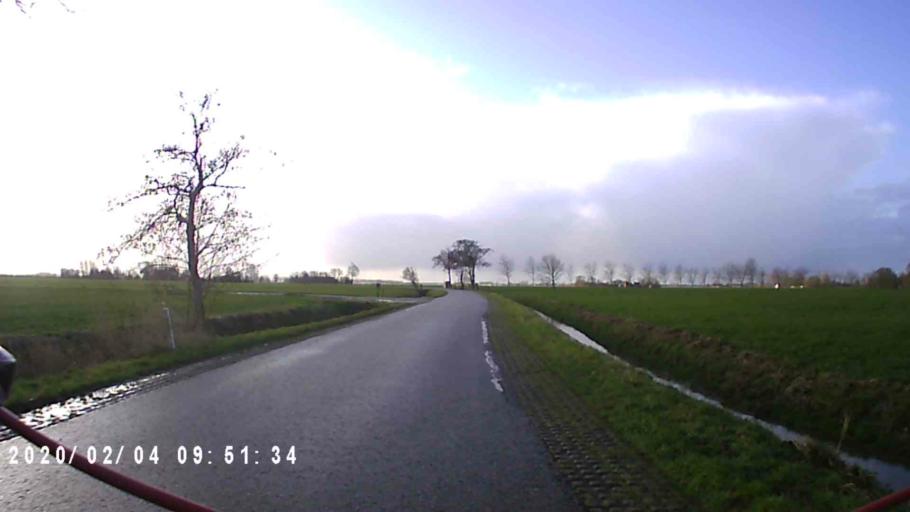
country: NL
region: Groningen
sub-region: Gemeente Zuidhorn
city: Aduard
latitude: 53.2870
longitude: 6.4944
